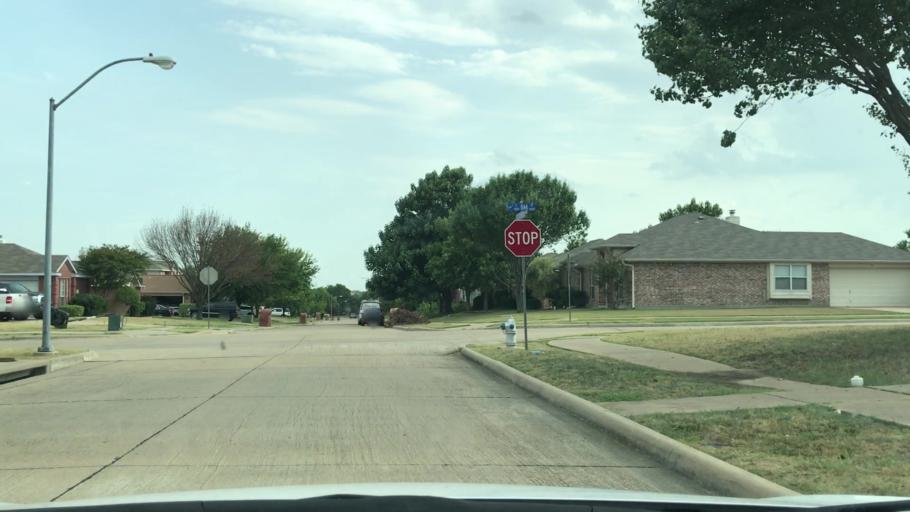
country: US
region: Texas
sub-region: Collin County
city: Wylie
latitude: 33.0143
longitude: -96.5177
